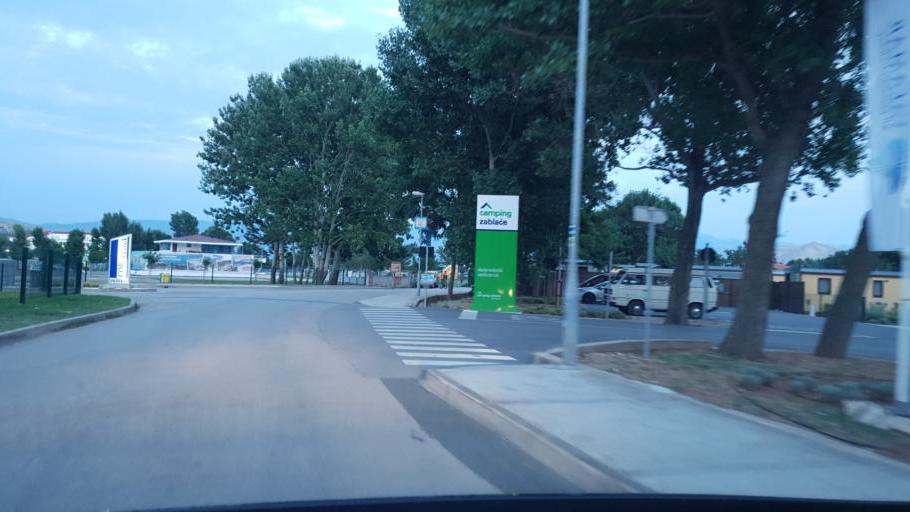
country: HR
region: Primorsko-Goranska
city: Punat
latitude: 44.9672
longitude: 14.7451
